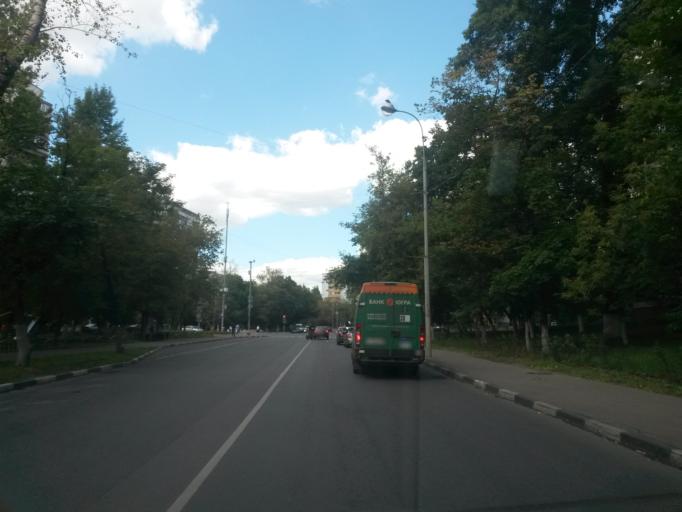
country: RU
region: Moscow
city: Tekstil'shchiki
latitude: 55.6843
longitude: 37.7242
